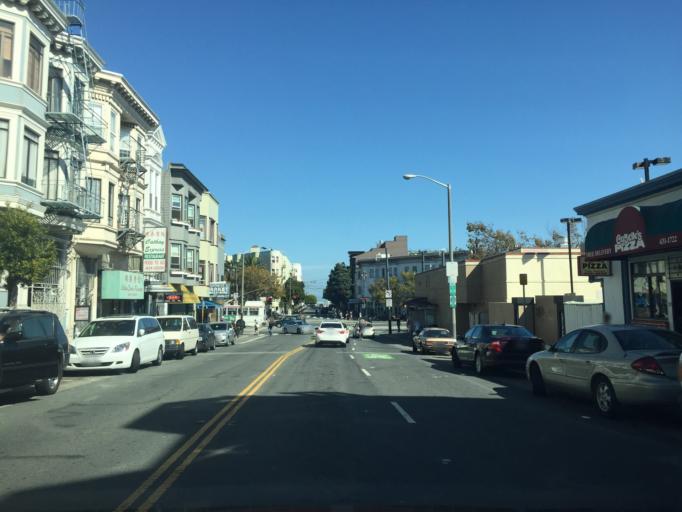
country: US
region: California
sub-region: San Francisco County
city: San Francisco
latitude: 37.7677
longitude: -122.4298
